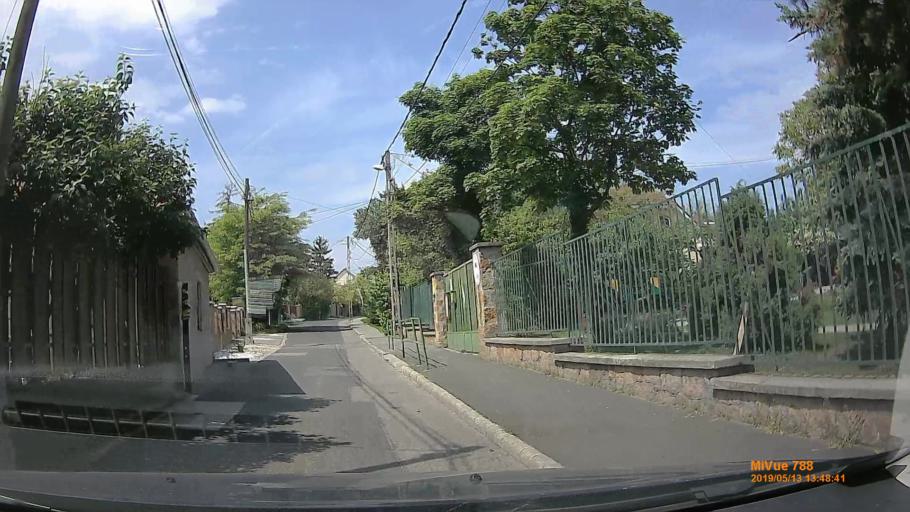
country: HU
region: Budapest
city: Budapest XXII. keruelet
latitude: 47.4171
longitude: 19.0139
